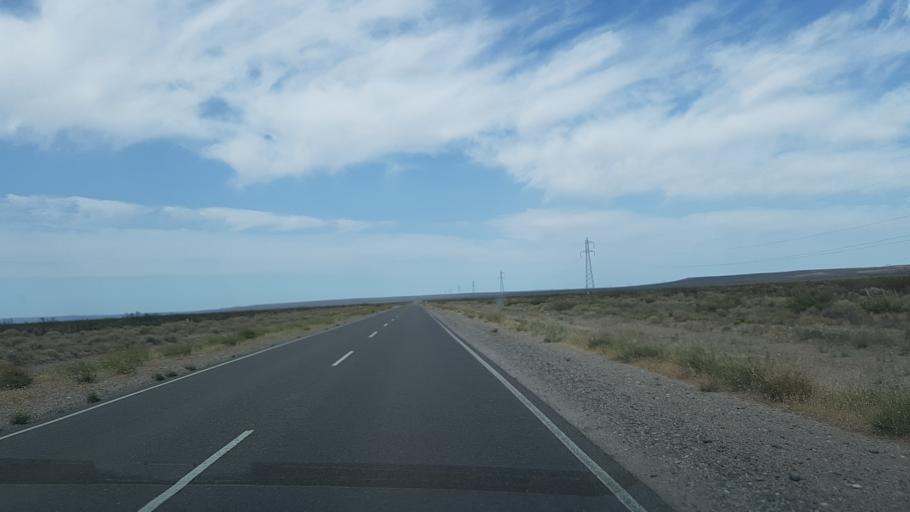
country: AR
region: Neuquen
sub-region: Departamento de Picun Leufu
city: Picun Leufu
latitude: -39.6668
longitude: -69.4368
